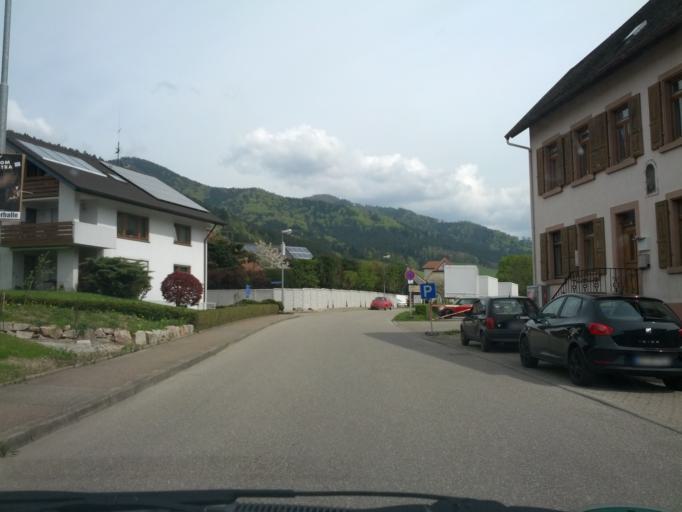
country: DE
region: Baden-Wuerttemberg
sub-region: Freiburg Region
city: Gutach im Breisgau
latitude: 48.1215
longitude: 8.0093
